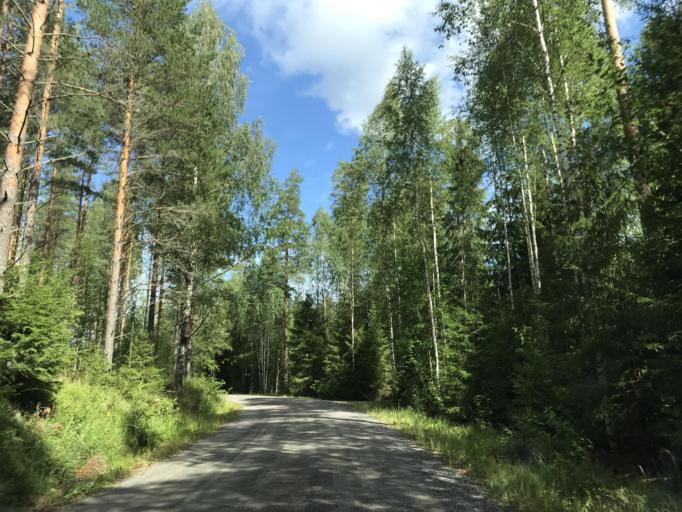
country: FI
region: Uusimaa
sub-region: Helsinki
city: Kaerkoelae
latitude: 60.6347
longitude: 23.7800
